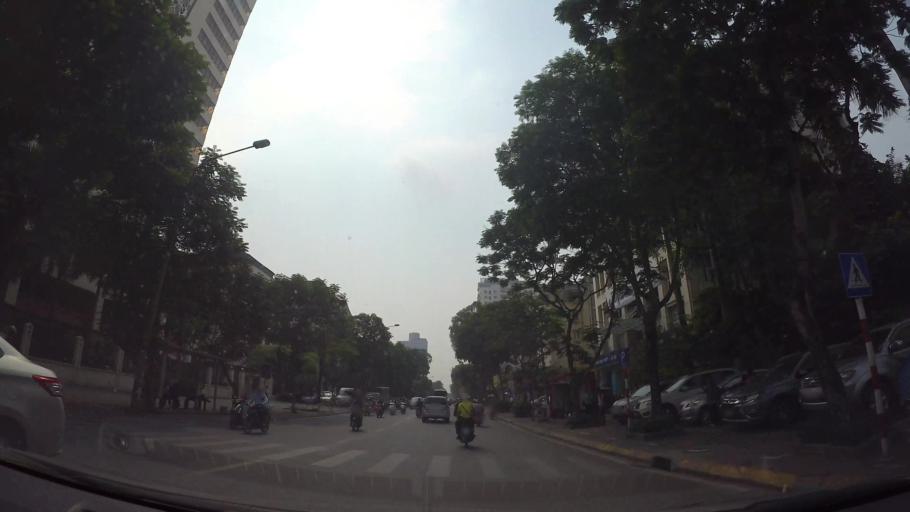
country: VN
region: Ha Noi
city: Cau Giay
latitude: 21.0192
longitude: 105.8095
